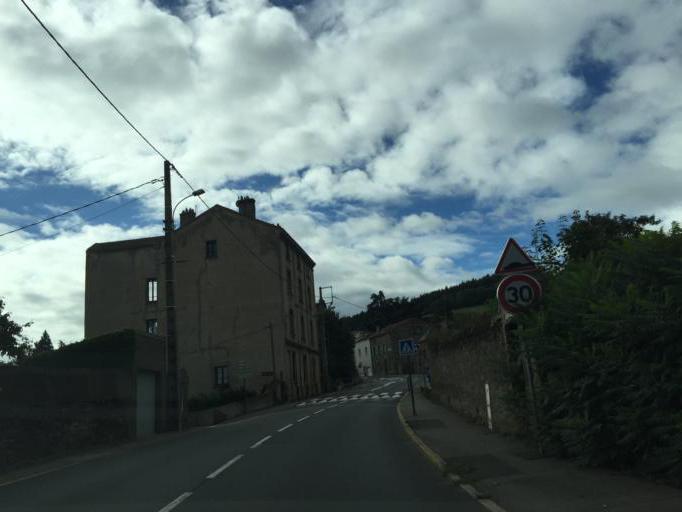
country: FR
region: Rhone-Alpes
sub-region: Departement de la Loire
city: Saint-Paul-en-Jarez
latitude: 45.4842
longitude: 4.5764
